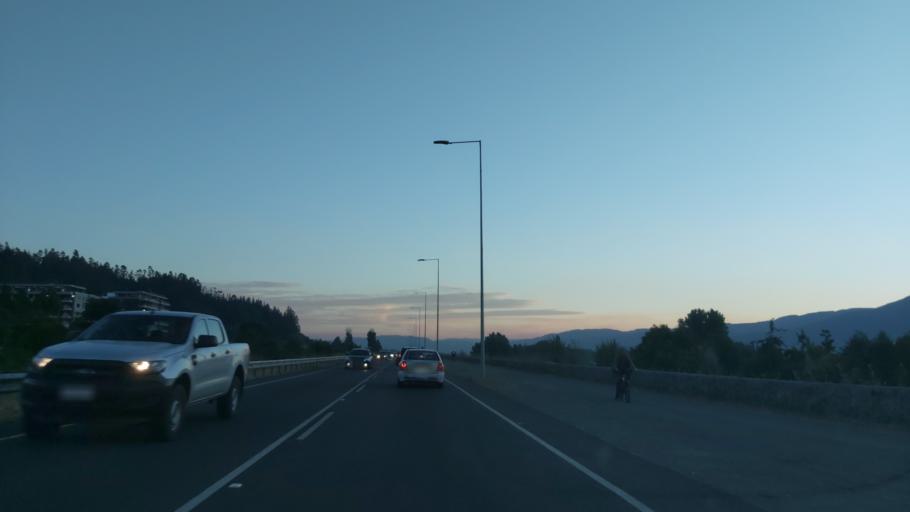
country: CL
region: Biobio
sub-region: Provincia de Concepcion
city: Chiguayante
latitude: -36.8801
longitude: -73.0389
